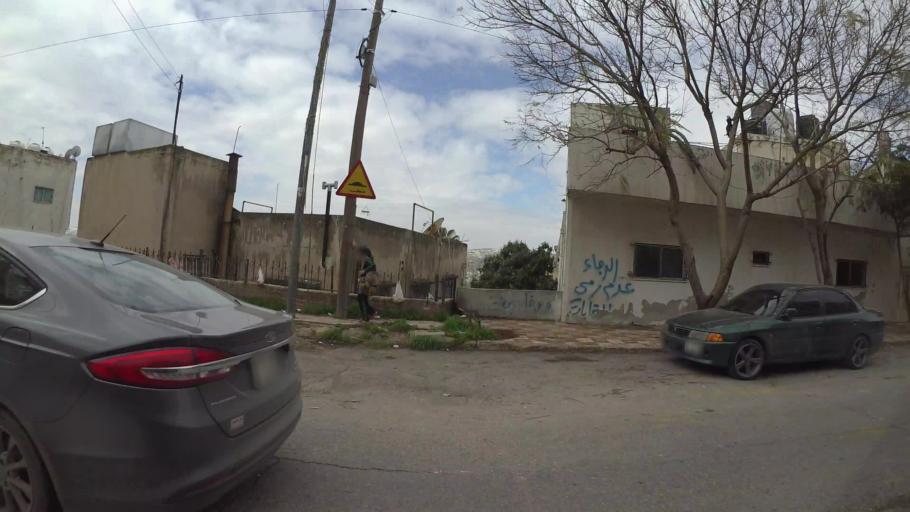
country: JO
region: Amman
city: Wadi as Sir
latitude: 31.9528
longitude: 35.8252
